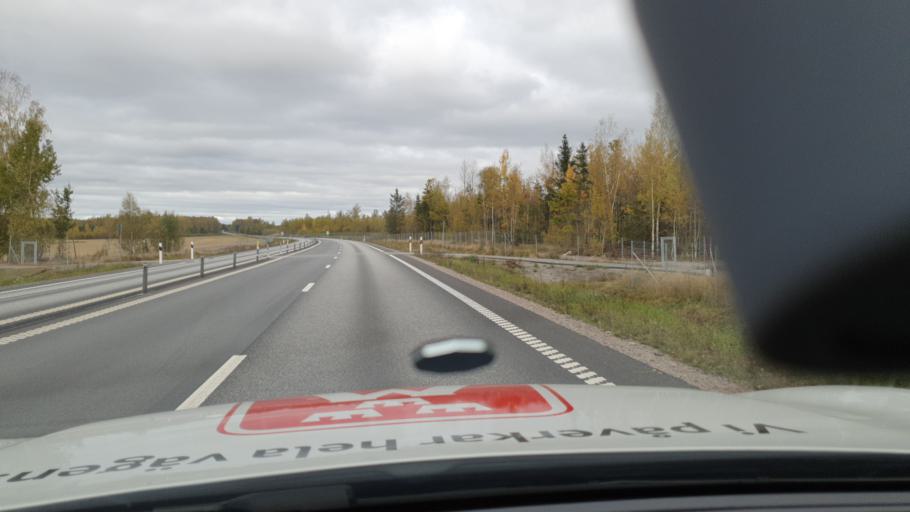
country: SE
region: OErebro
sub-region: Hallsbergs Kommun
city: Skollersta
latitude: 59.1079
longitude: 15.3060
